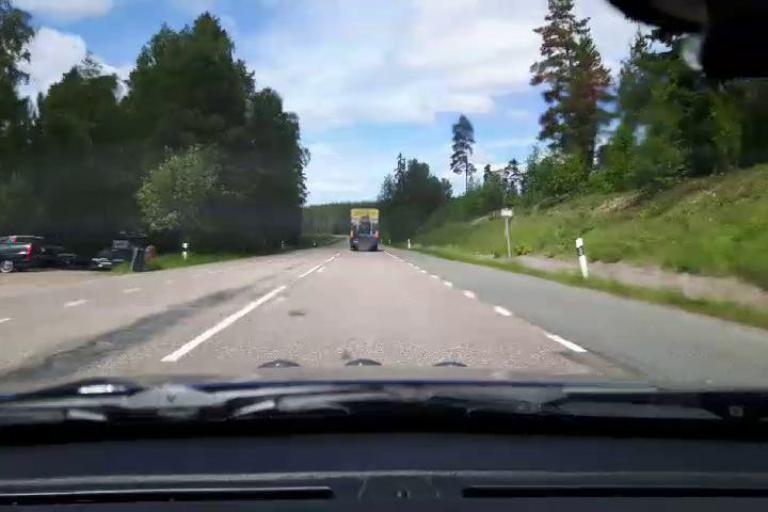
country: SE
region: Uppsala
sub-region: Osthammars Kommun
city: Bjorklinge
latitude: 60.0964
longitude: 17.5539
